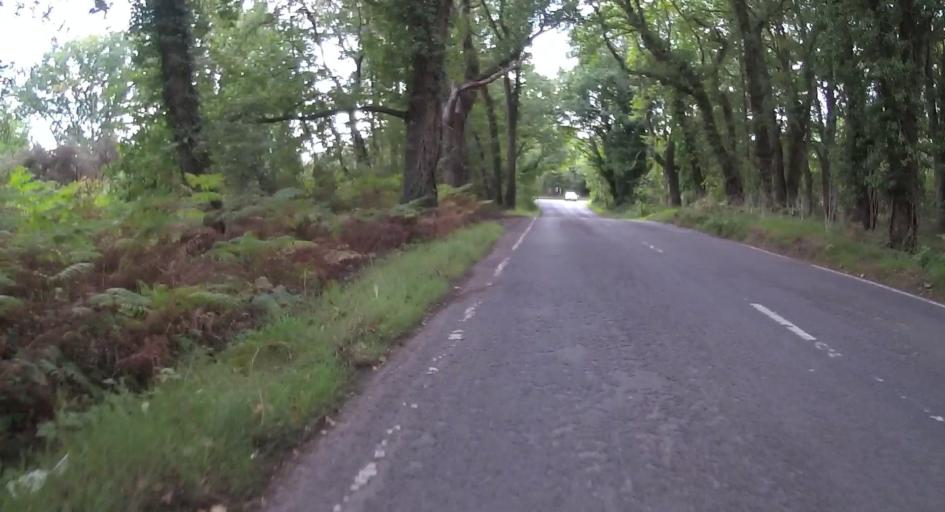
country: GB
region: England
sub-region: Surrey
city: Chobham
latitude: 51.3648
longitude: -0.6090
